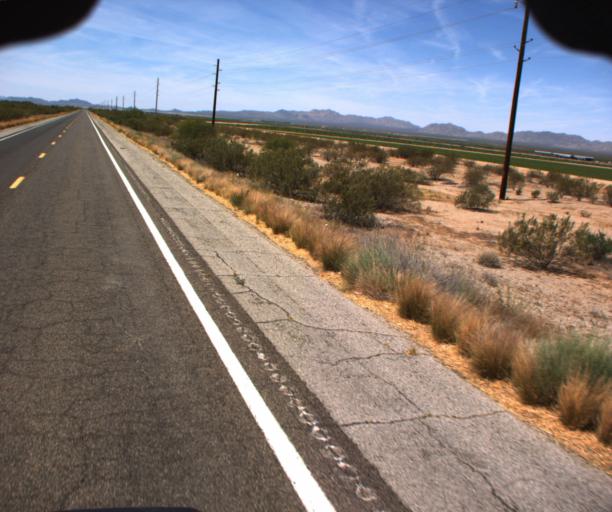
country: US
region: Arizona
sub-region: La Paz County
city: Salome
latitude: 33.8427
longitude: -113.4727
